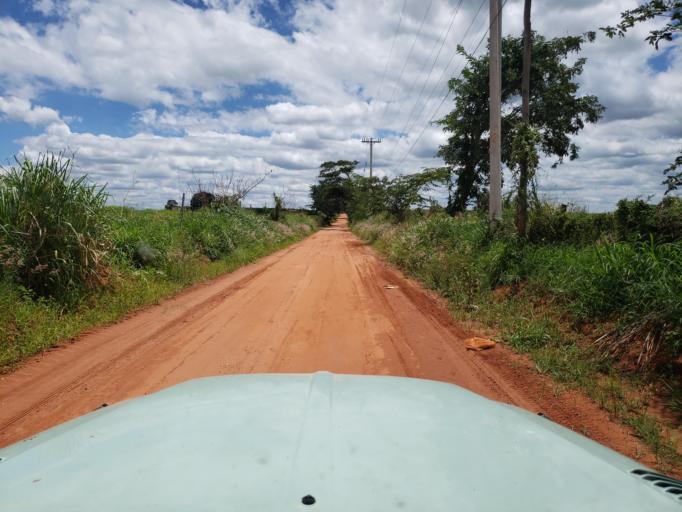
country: BR
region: Sao Paulo
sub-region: Aguai
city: Aguai
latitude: -22.1996
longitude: -46.9575
